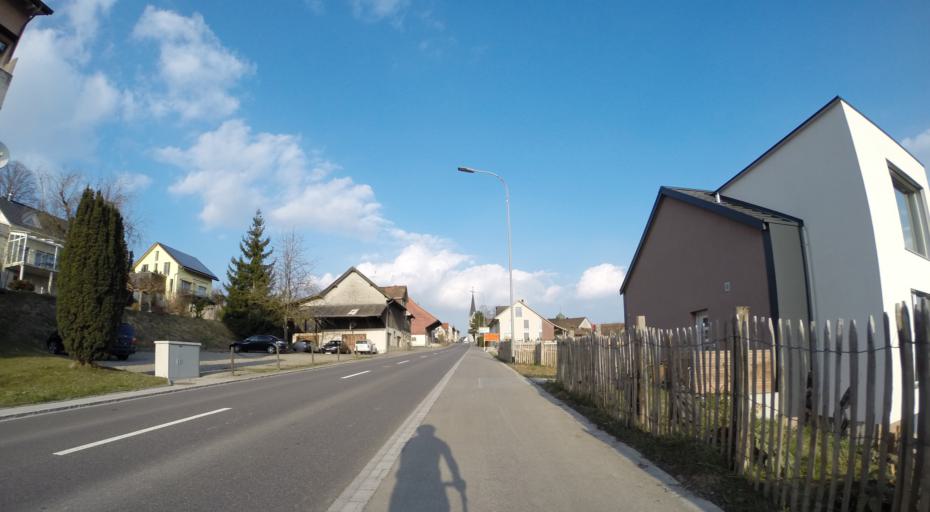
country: CH
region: Thurgau
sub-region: Frauenfeld District
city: Huttwilen
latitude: 47.6039
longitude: 8.9057
